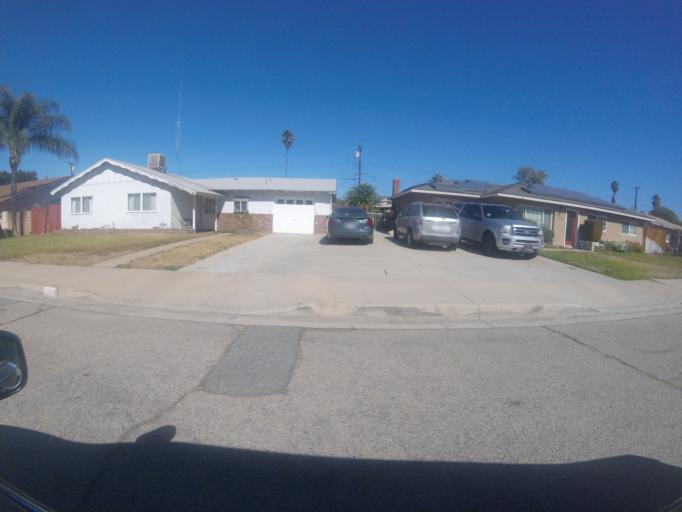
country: US
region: California
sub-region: San Bernardino County
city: Redlands
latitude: 34.0709
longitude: -117.1704
